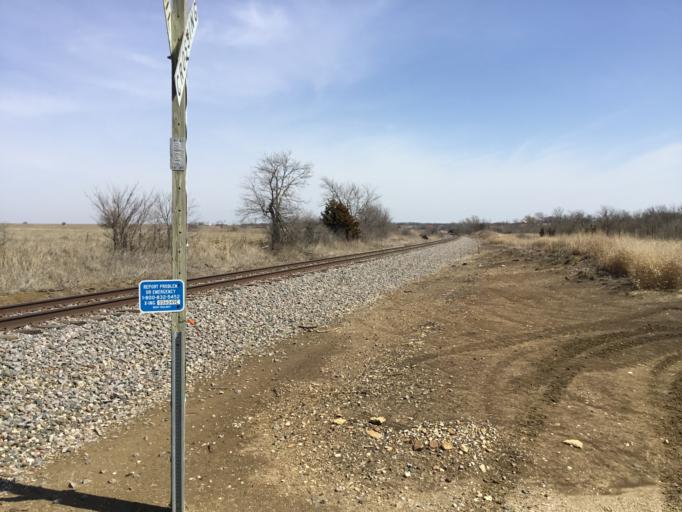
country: US
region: Kansas
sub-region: Lyon County
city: Emporia
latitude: 38.5066
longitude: -95.9961
